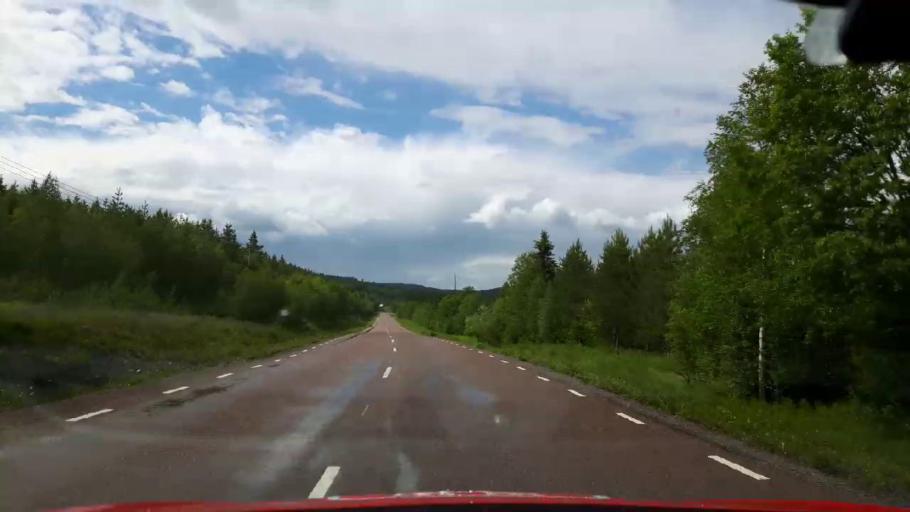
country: SE
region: Jaemtland
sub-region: Krokoms Kommun
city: Valla
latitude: 63.9005
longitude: 14.2365
